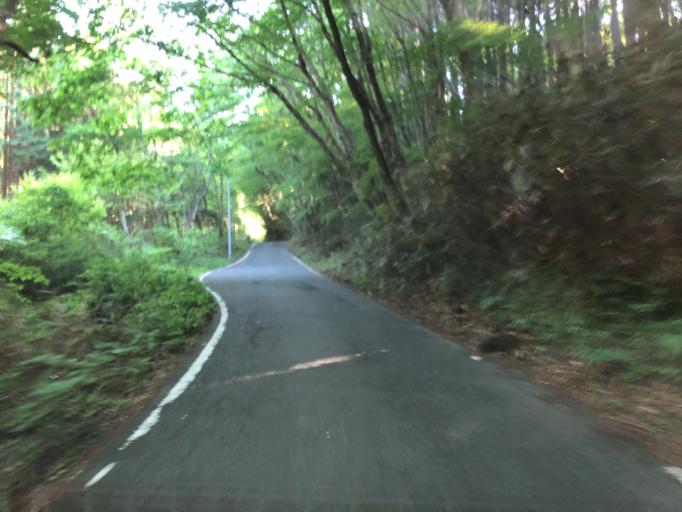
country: JP
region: Ibaraki
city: Kitaibaraki
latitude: 36.8948
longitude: 140.6111
